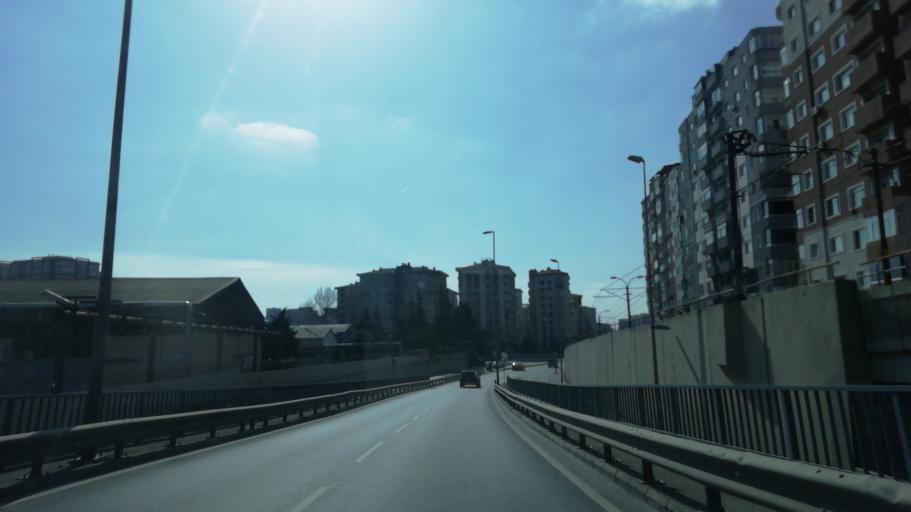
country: TR
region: Istanbul
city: merter keresteciler
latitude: 41.0191
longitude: 28.9009
